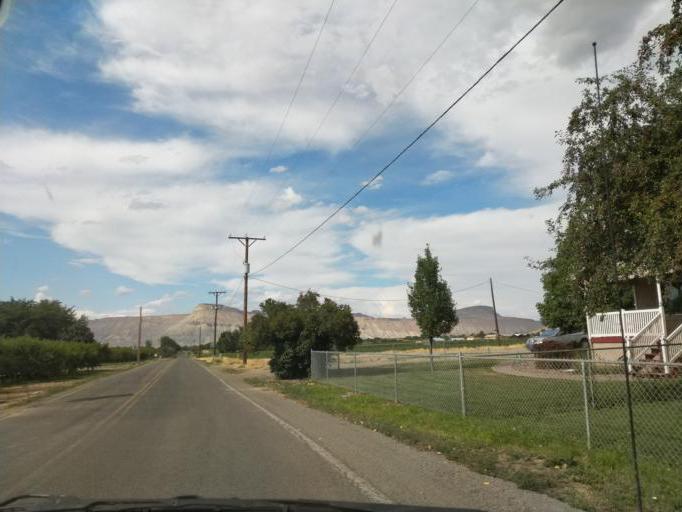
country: US
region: Colorado
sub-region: Mesa County
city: Clifton
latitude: 39.0558
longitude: -108.4133
